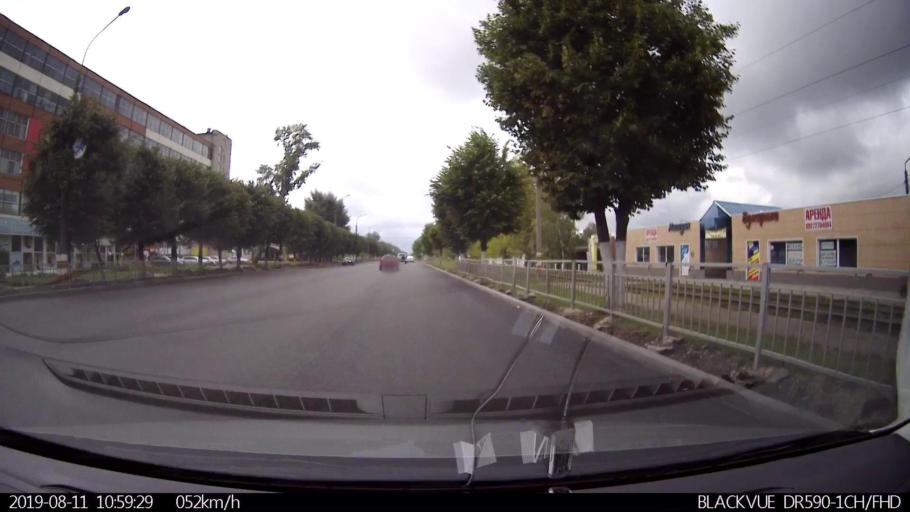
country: RU
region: Ulyanovsk
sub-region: Ulyanovskiy Rayon
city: Ulyanovsk
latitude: 54.2499
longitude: 48.3152
